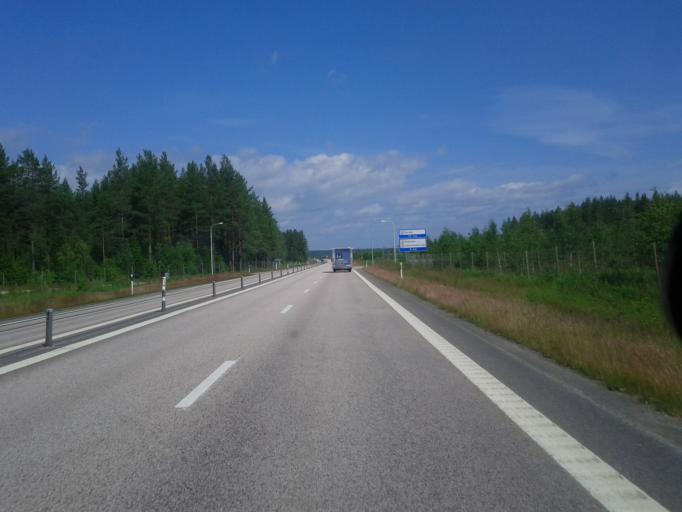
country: SE
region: Vaesterbotten
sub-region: Nordmalings Kommun
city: Nordmaling
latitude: 63.5529
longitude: 19.4186
